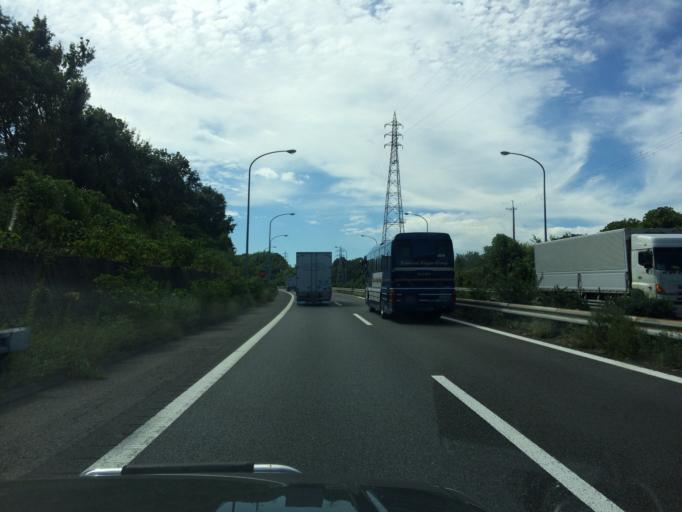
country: JP
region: Osaka
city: Izumi
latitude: 34.4464
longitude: 135.4446
